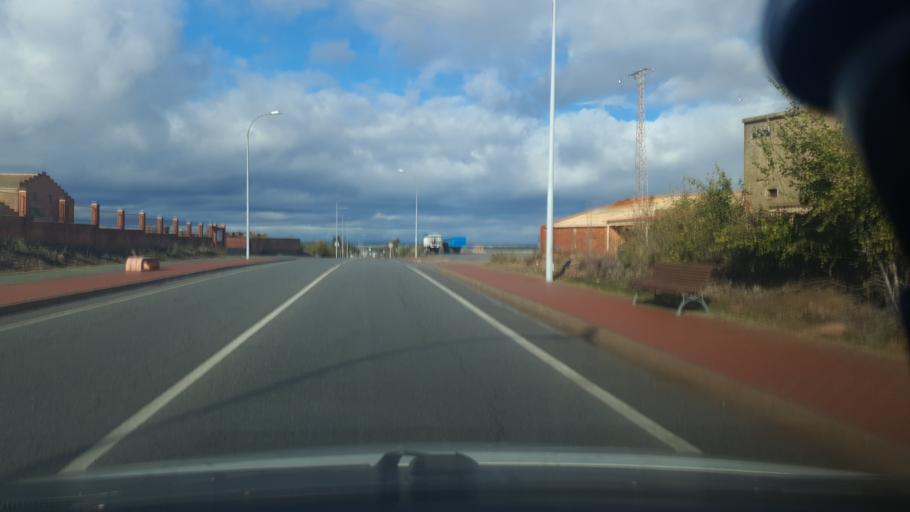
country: ES
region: Castille and Leon
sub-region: Provincia de Segovia
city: Carbonero el Mayor
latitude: 41.1277
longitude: -4.2687
